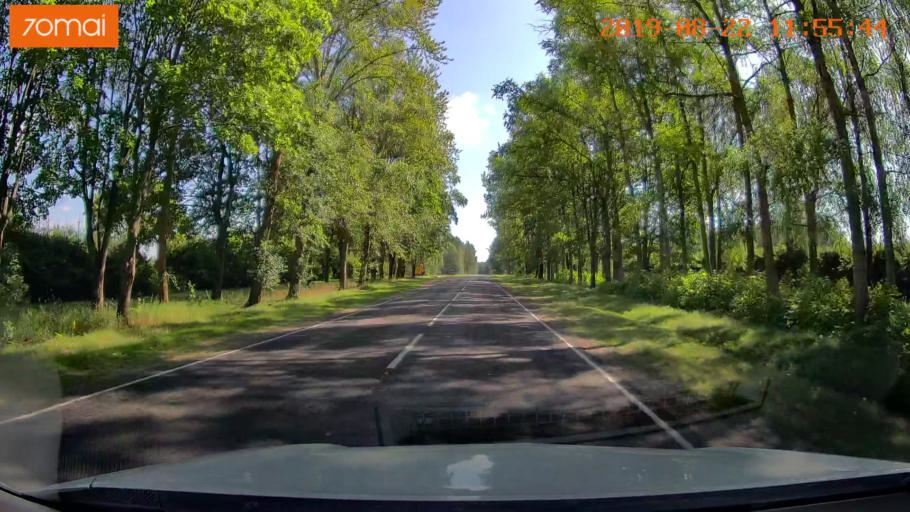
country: BY
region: Minsk
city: Prawdzinski
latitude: 53.4306
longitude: 27.5547
